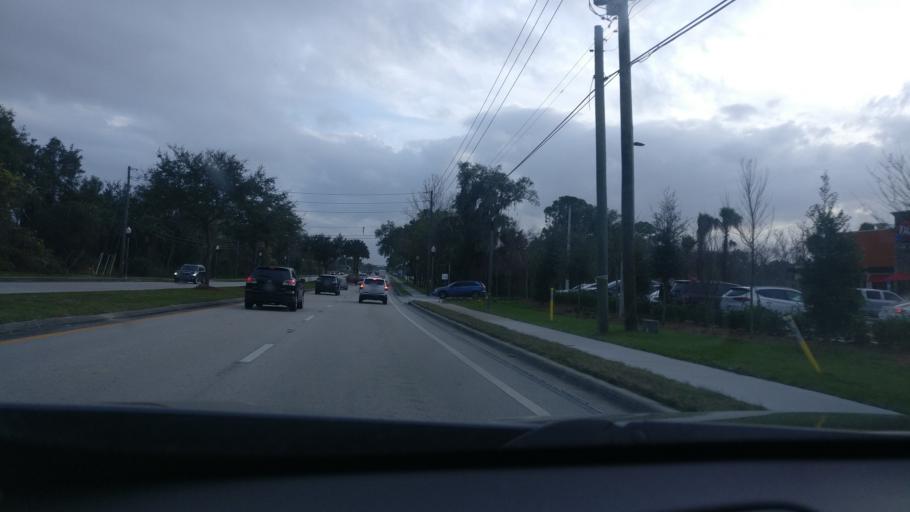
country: US
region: Florida
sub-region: Volusia County
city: DeBary
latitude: 28.8955
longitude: -81.3056
